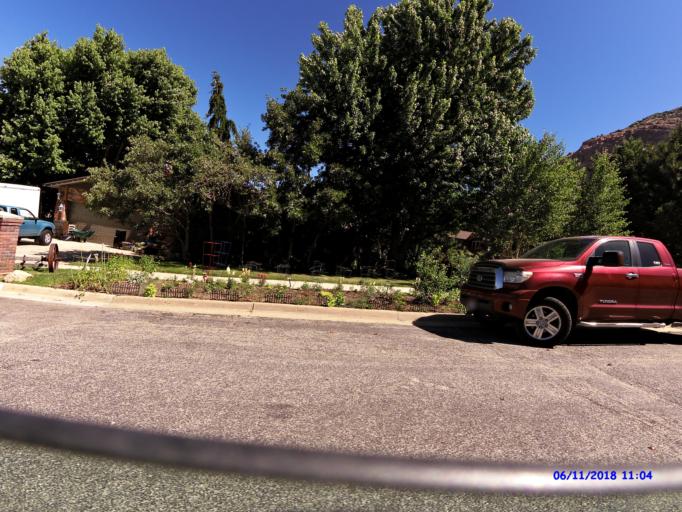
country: US
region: Utah
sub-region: Weber County
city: Ogden
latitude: 41.2180
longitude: -111.9306
